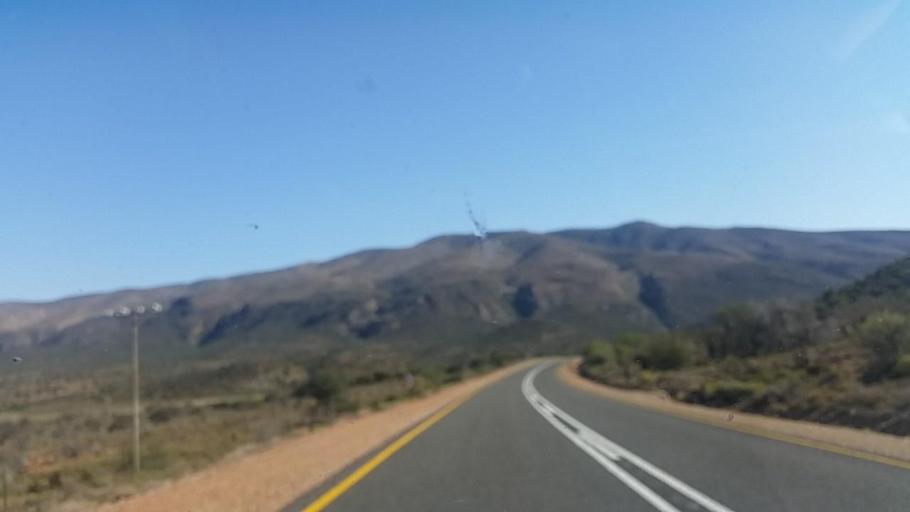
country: ZA
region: Eastern Cape
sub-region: Cacadu District Municipality
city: Willowmore
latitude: -33.4265
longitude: 23.3056
